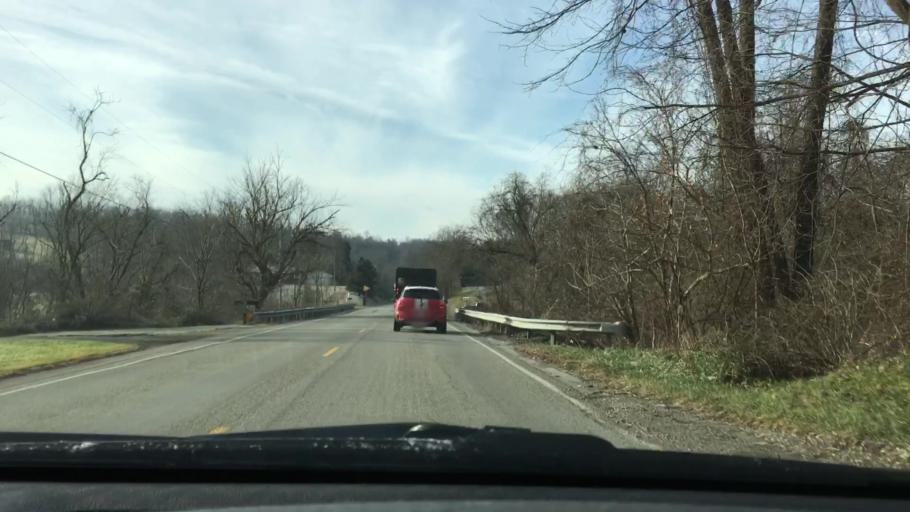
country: US
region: Pennsylvania
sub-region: Allegheny County
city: Industry
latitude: 40.2468
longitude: -79.7815
